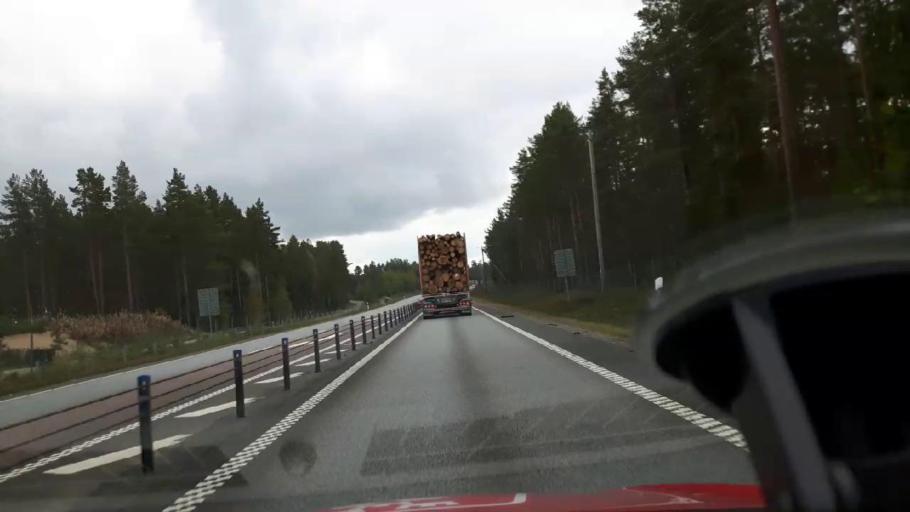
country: SE
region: Gaevleborg
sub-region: Gavle Kommun
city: Norrsundet
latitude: 61.0337
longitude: 16.9714
